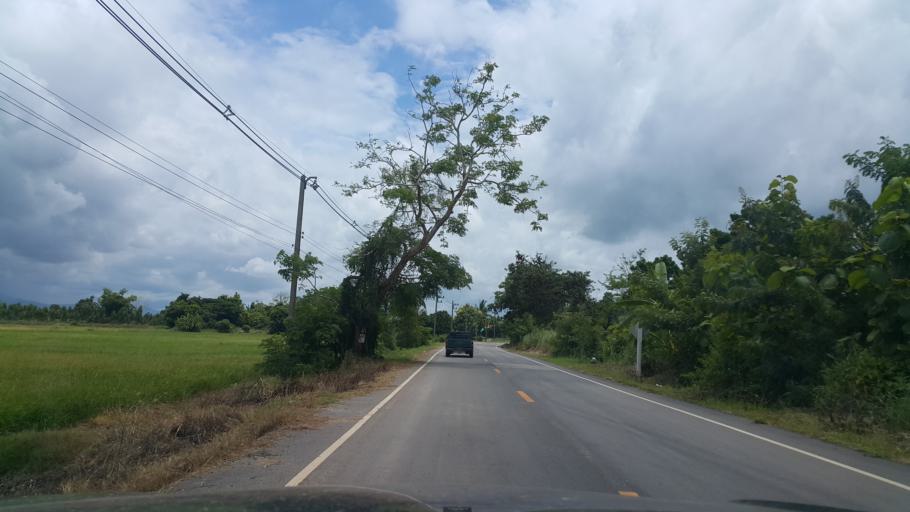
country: TH
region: Sukhothai
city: Kong Krailat
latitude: 16.9330
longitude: 99.9381
